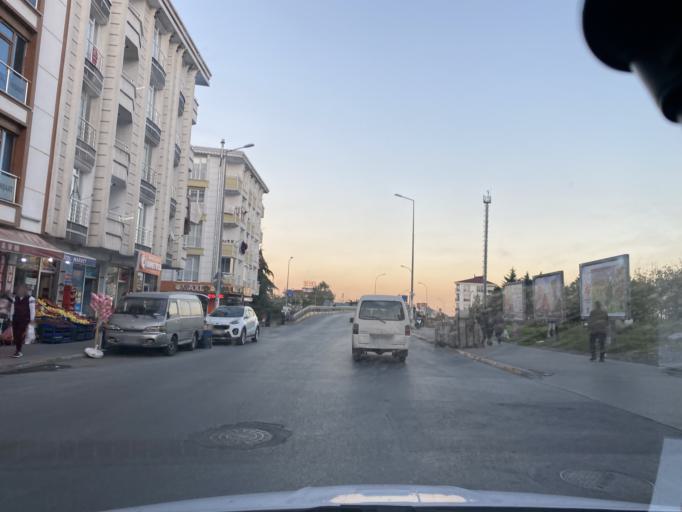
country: TR
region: Istanbul
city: Esenyurt
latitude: 41.0337
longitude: 28.6856
